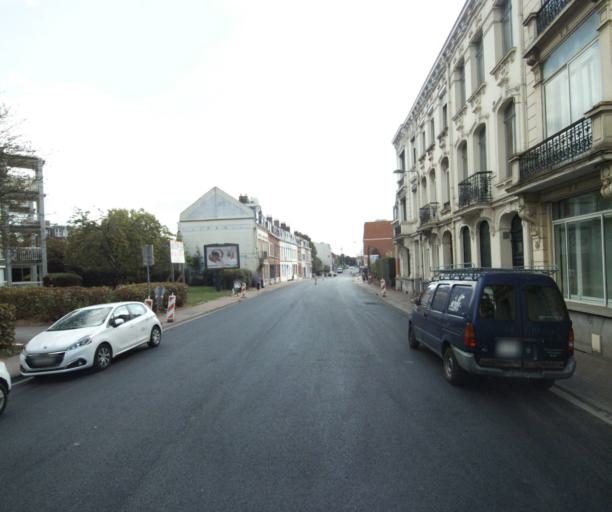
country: FR
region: Nord-Pas-de-Calais
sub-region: Departement du Nord
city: La Madeleine
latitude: 50.6423
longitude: 3.0891
